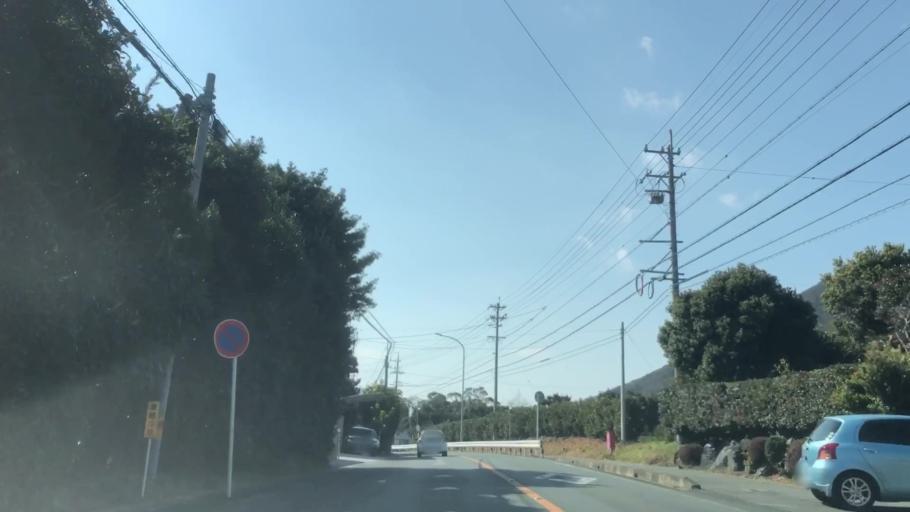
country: JP
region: Aichi
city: Tahara
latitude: 34.6581
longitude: 137.2481
